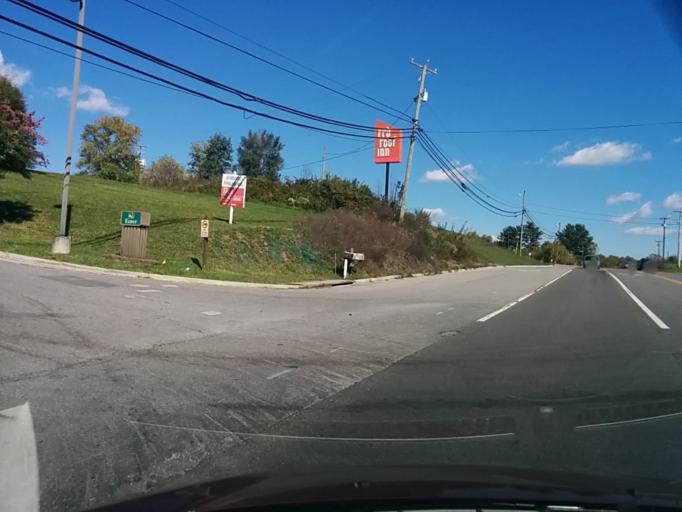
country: US
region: Virginia
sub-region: Botetourt County
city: Daleville
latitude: 37.3913
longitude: -79.8998
